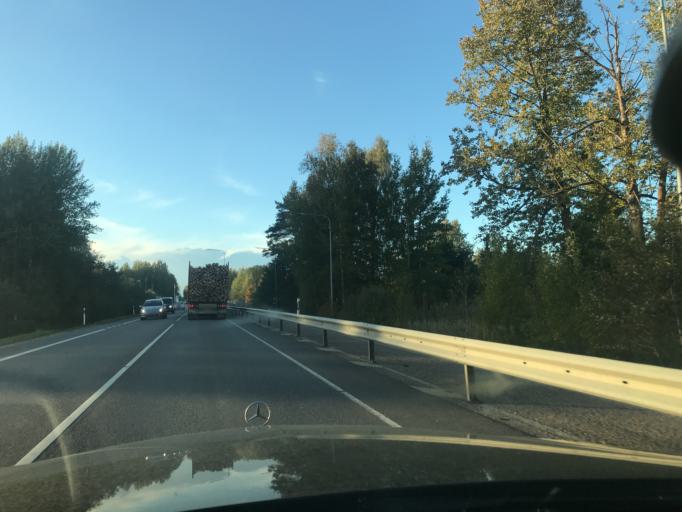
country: EE
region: Vorumaa
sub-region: Voru linn
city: Voru
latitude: 57.8599
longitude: 26.9713
